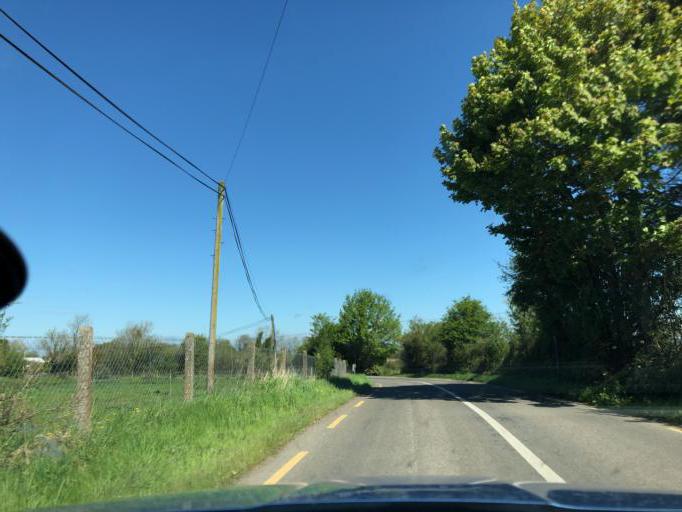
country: IE
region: Connaught
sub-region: County Galway
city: Portumna
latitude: 53.1290
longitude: -8.3509
